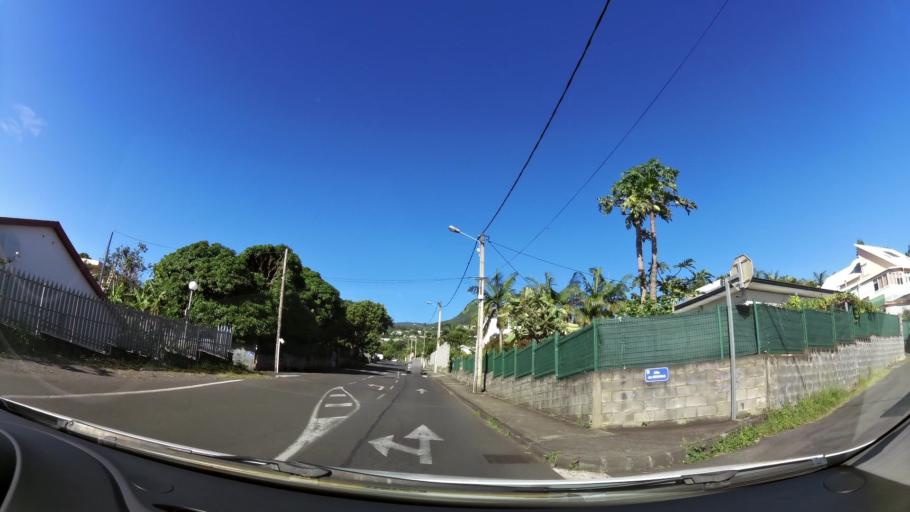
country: RE
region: Reunion
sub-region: Reunion
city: Saint-Denis
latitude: -20.9215
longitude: 55.4739
